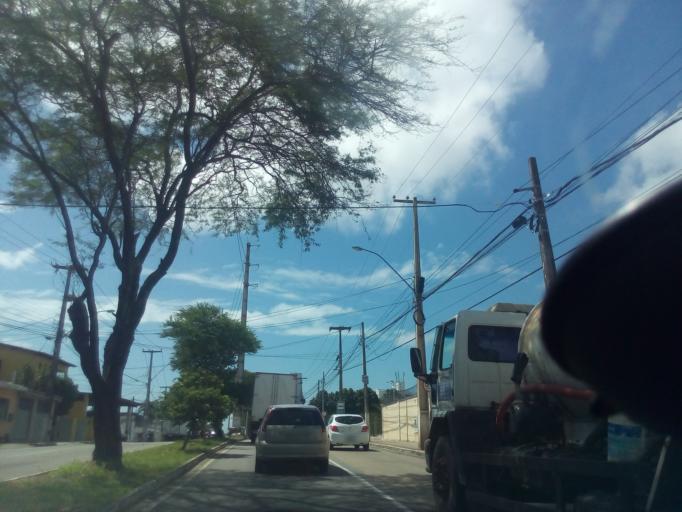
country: BR
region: Rio Grande do Norte
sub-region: Natal
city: Natal
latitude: -5.8234
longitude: -35.2275
